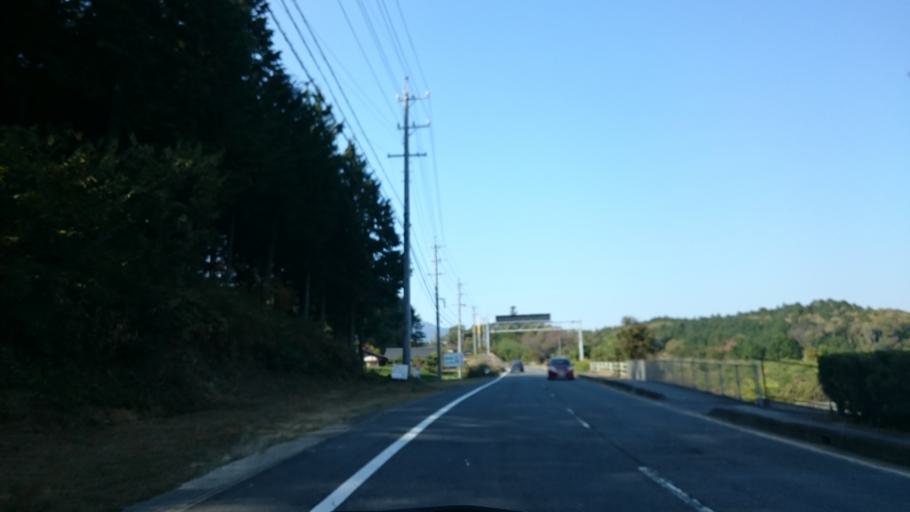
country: JP
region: Gifu
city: Nakatsugawa
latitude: 35.5283
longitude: 137.4636
